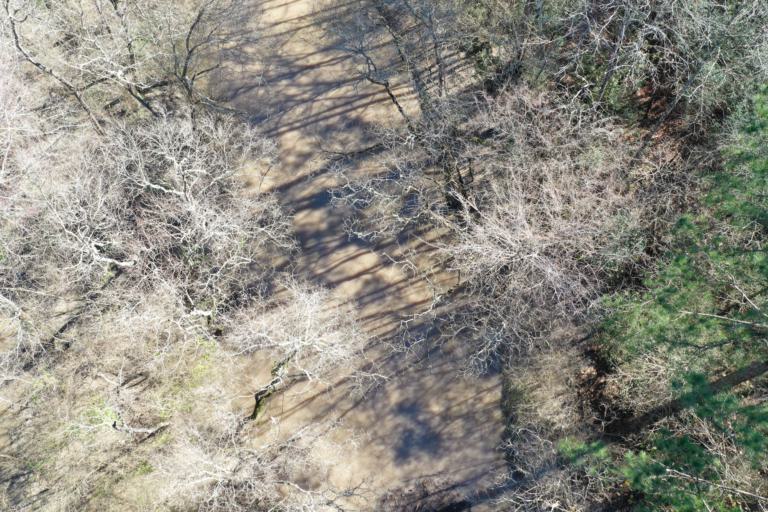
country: US
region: Louisiana
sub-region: Calcasieu Parish
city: Iowa
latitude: 30.3170
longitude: -93.0311
